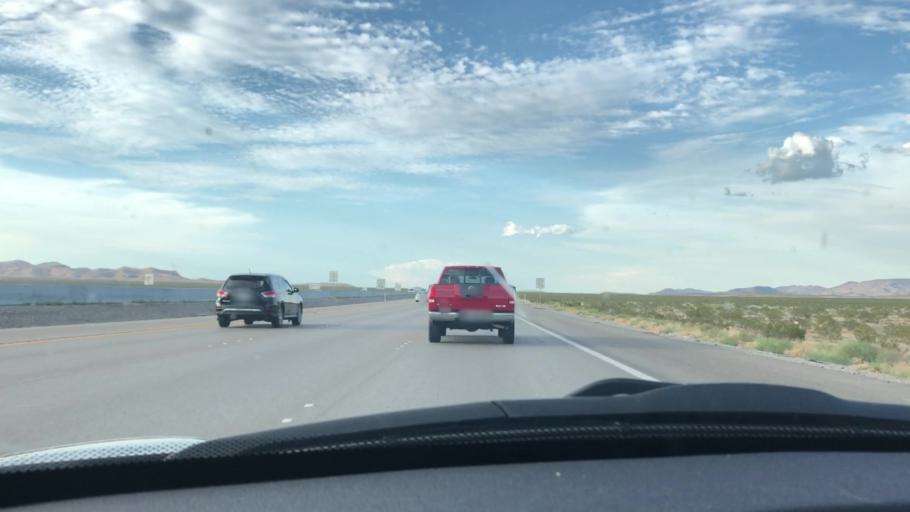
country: US
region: Nevada
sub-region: Clark County
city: Enterprise
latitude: 35.7860
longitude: -115.3241
